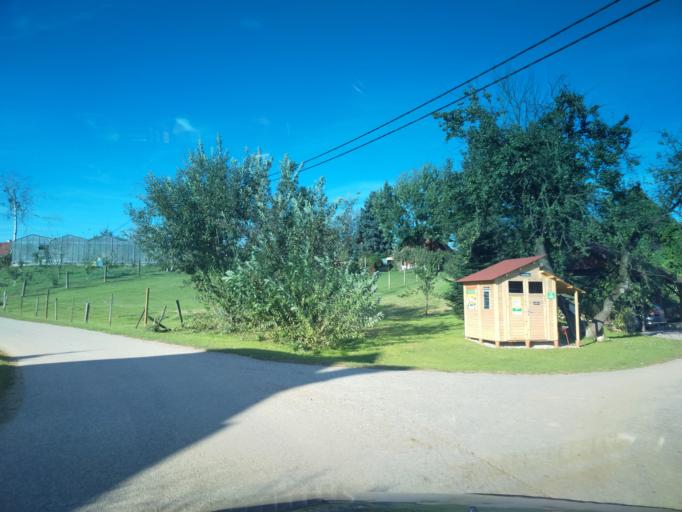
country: AT
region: Styria
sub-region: Politischer Bezirk Deutschlandsberg
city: Sankt Martin im Sulmtal
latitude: 46.7332
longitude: 15.3118
